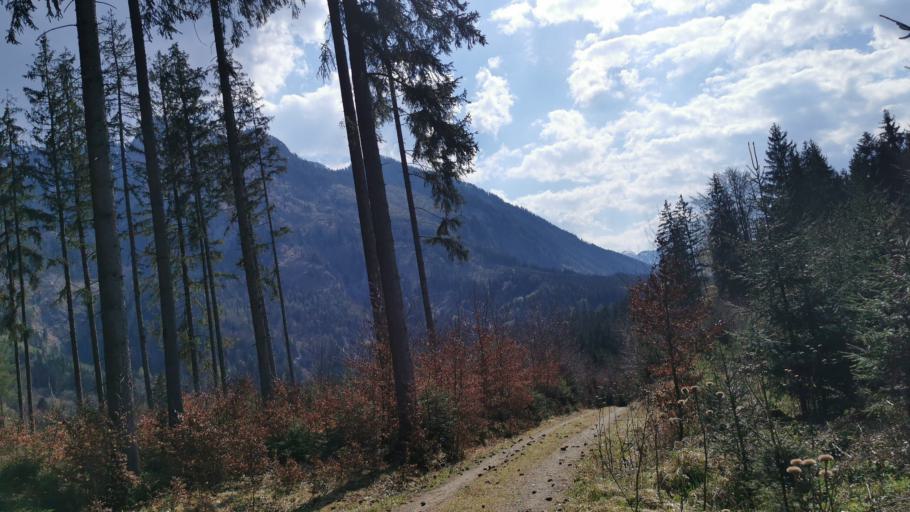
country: AT
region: Salzburg
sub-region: Politischer Bezirk Salzburg-Umgebung
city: Grodig
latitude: 47.7415
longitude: 12.9789
